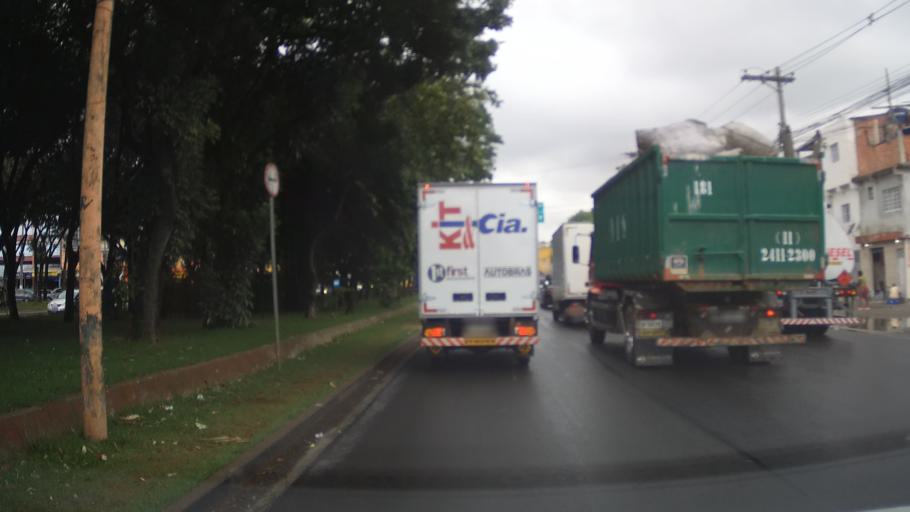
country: BR
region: Sao Paulo
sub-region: Guarulhos
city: Guarulhos
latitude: -23.4709
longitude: -46.4662
